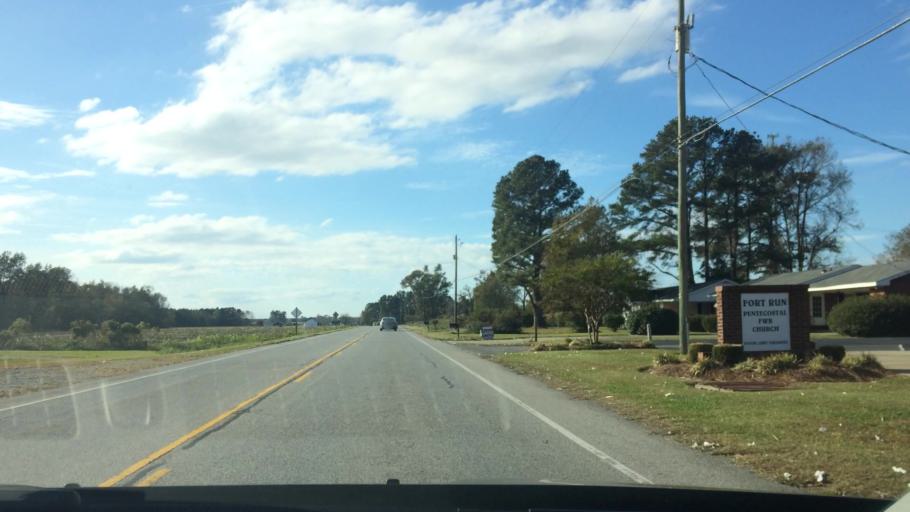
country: US
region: North Carolina
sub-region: Greene County
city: Snow Hill
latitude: 35.4407
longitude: -77.7927
